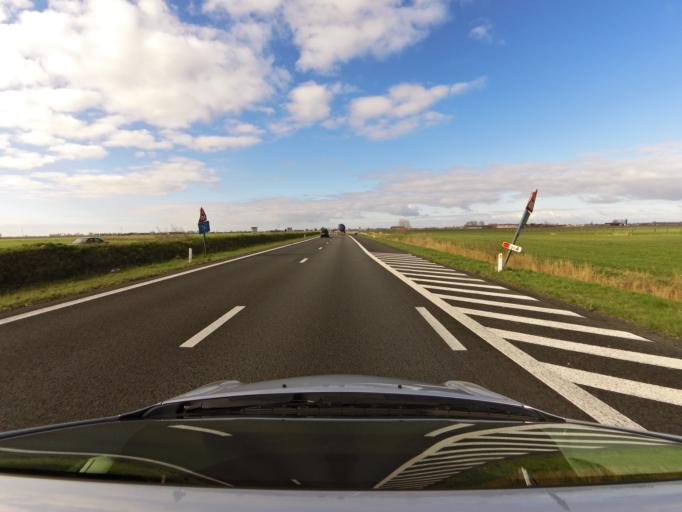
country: BE
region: Flanders
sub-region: Provincie West-Vlaanderen
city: Nieuwpoort
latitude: 51.1071
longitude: 2.7461
